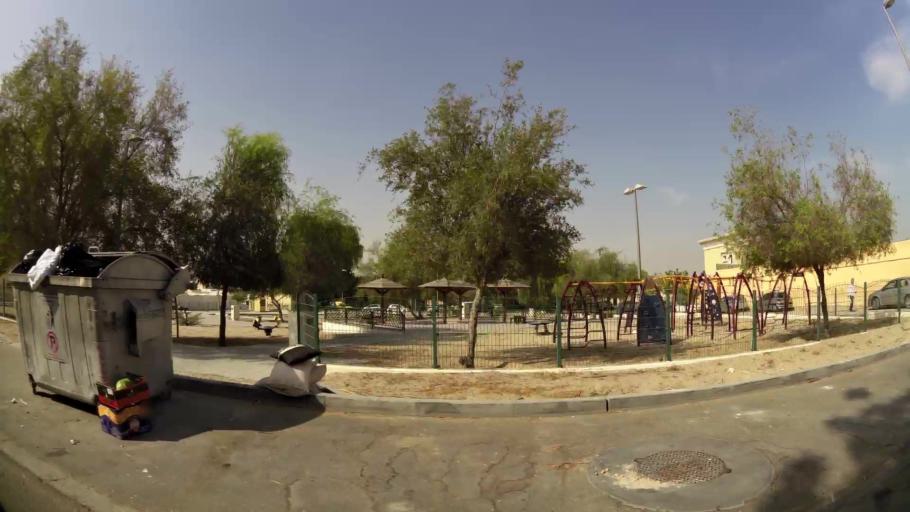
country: AE
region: Ash Shariqah
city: Sharjah
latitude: 25.2218
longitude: 55.3905
